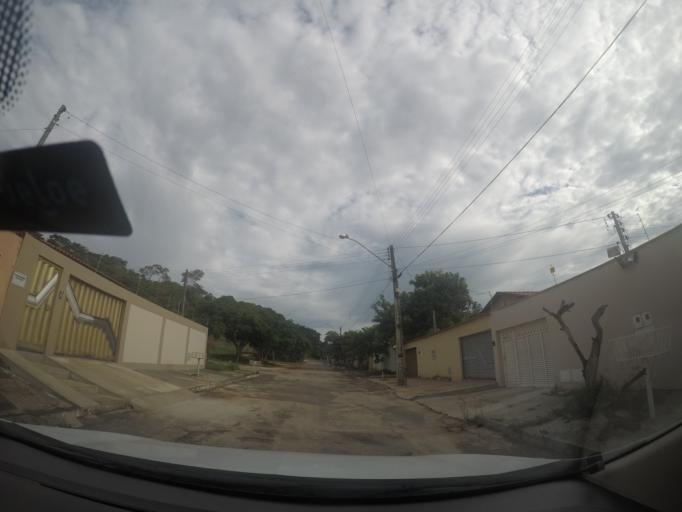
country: BR
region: Goias
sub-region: Goiania
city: Goiania
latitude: -16.6886
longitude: -49.2004
